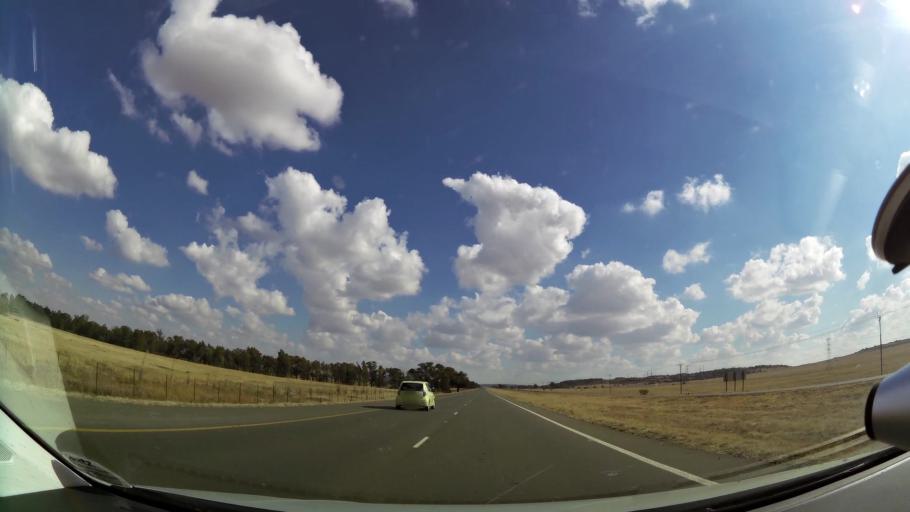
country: ZA
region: Orange Free State
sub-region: Mangaung Metropolitan Municipality
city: Bloemfontein
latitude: -29.1349
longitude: 26.1333
